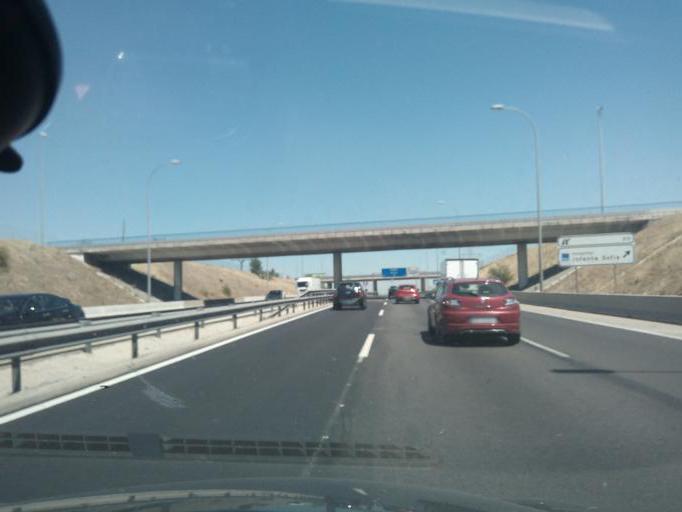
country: ES
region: Madrid
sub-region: Provincia de Madrid
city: San Sebastian de los Reyes
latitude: 40.5457
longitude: -3.6080
